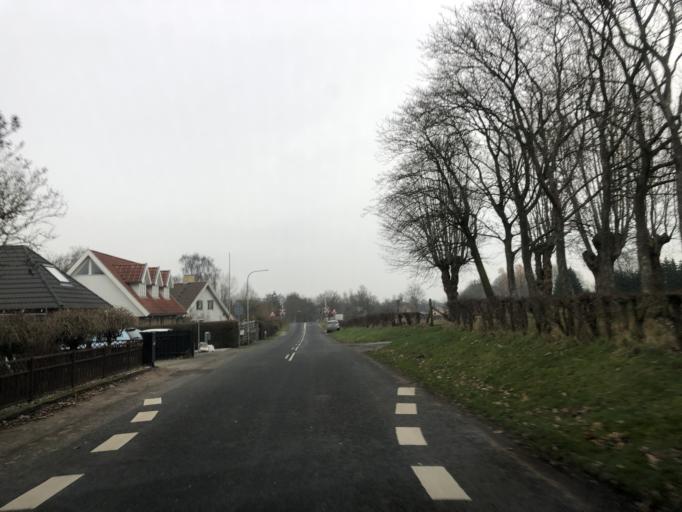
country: DK
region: South Denmark
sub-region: Faaborg-Midtfyn Kommune
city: Arslev
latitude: 55.2986
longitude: 10.4686
